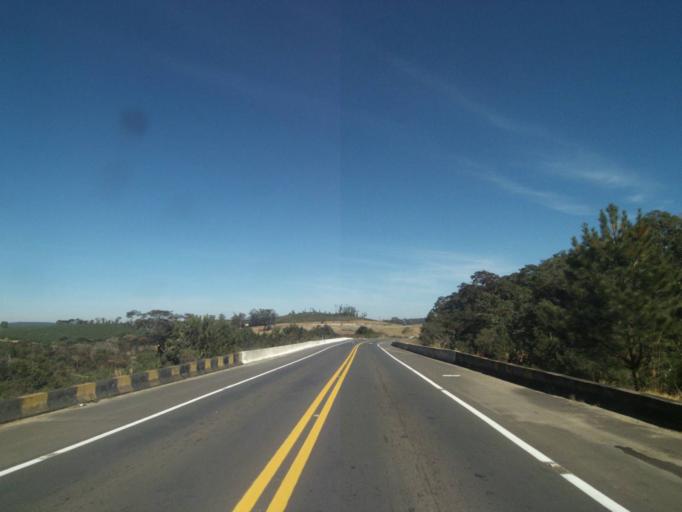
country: BR
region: Parana
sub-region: Tibagi
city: Tibagi
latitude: -24.8119
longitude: -50.4834
